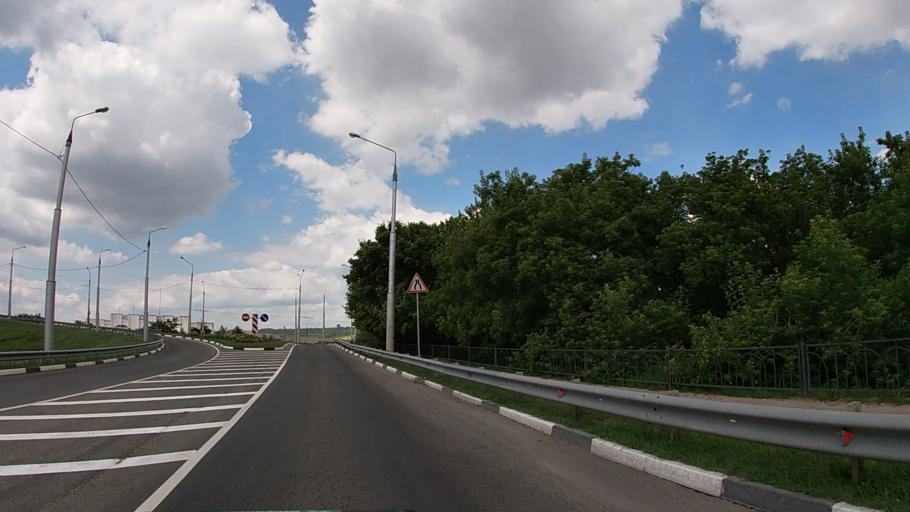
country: RU
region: Belgorod
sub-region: Belgorodskiy Rayon
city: Belgorod
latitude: 50.5897
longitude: 36.5670
